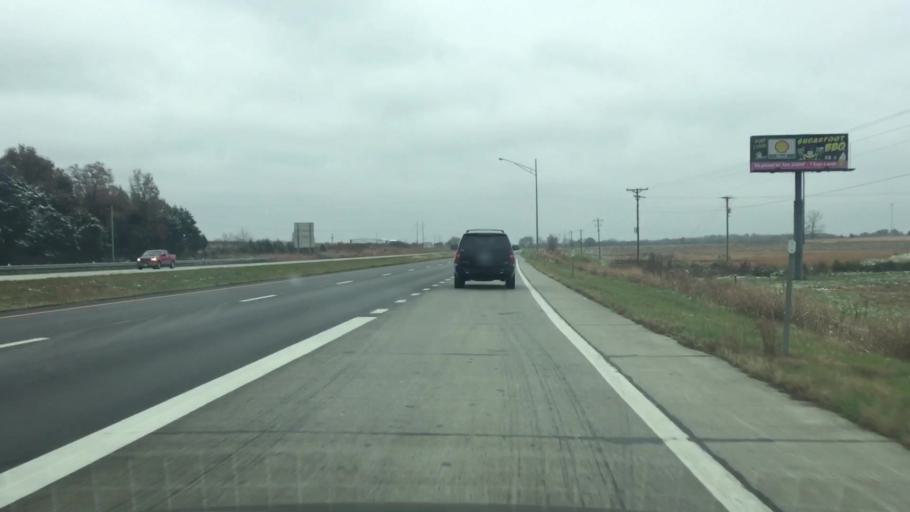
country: US
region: Missouri
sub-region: Saint Clair County
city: Osceola
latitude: 38.0377
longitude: -93.6801
